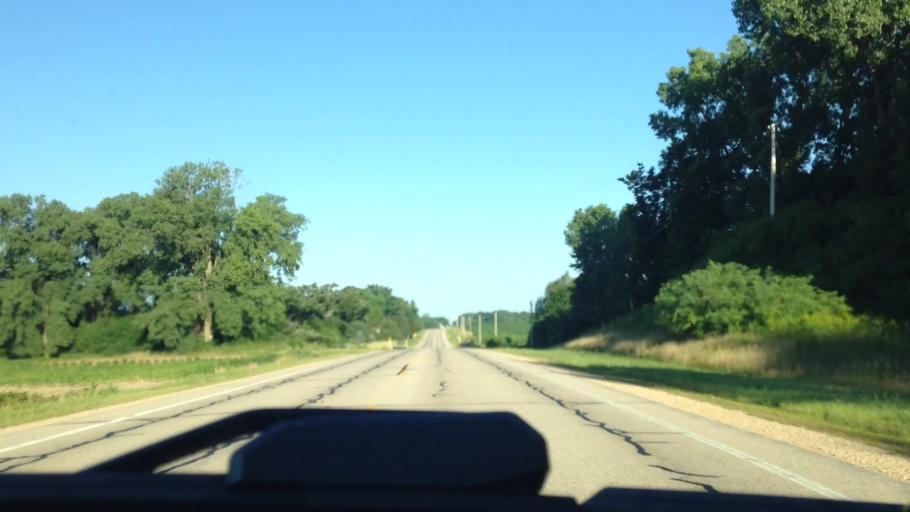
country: US
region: Wisconsin
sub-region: Columbia County
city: Fall River
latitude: 43.3407
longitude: -89.1248
